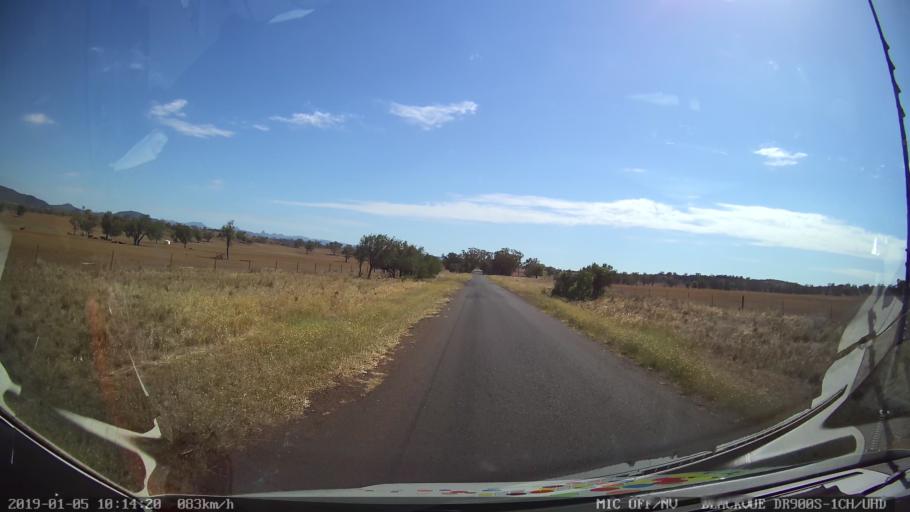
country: AU
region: New South Wales
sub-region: Gilgandra
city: Gilgandra
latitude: -31.5939
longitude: 148.9333
